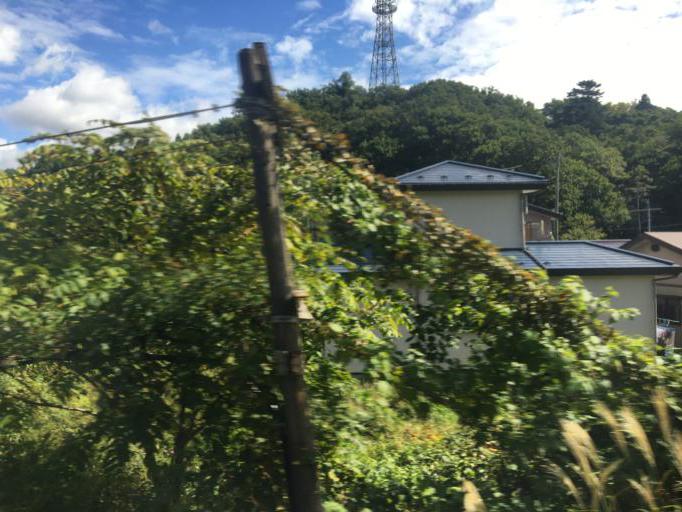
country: JP
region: Akita
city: Akita
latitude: 39.7039
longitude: 140.1263
